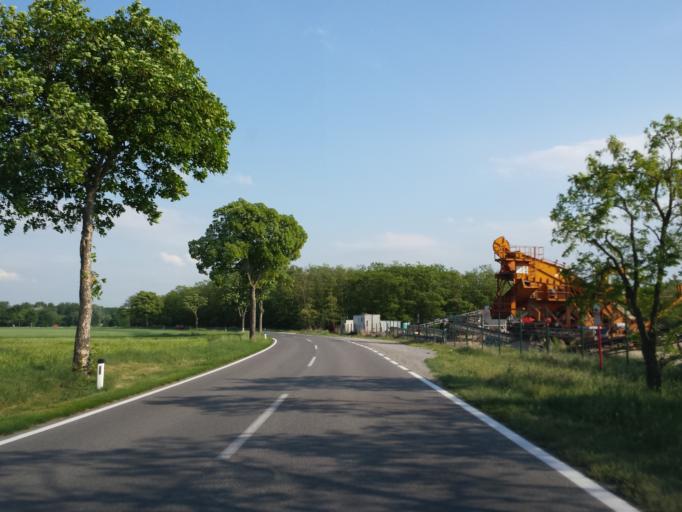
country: AT
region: Lower Austria
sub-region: Politischer Bezirk Ganserndorf
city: Marchegg
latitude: 48.2928
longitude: 16.8762
